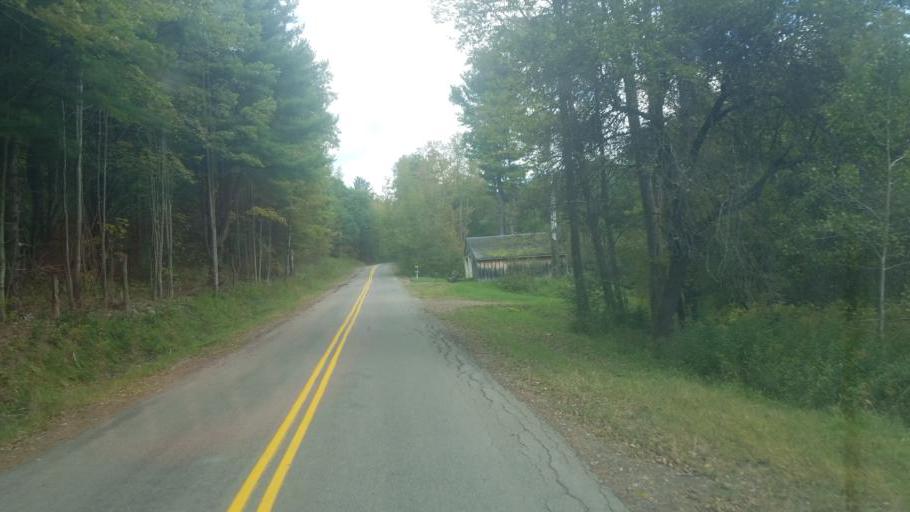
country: US
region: New York
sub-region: Allegany County
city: Cuba
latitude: 42.2207
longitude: -78.3603
